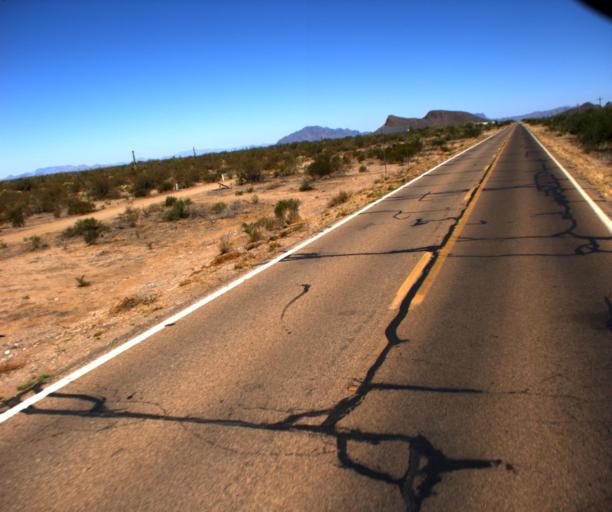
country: US
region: Arizona
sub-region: Pima County
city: Sells
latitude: 31.9281
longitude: -111.9034
